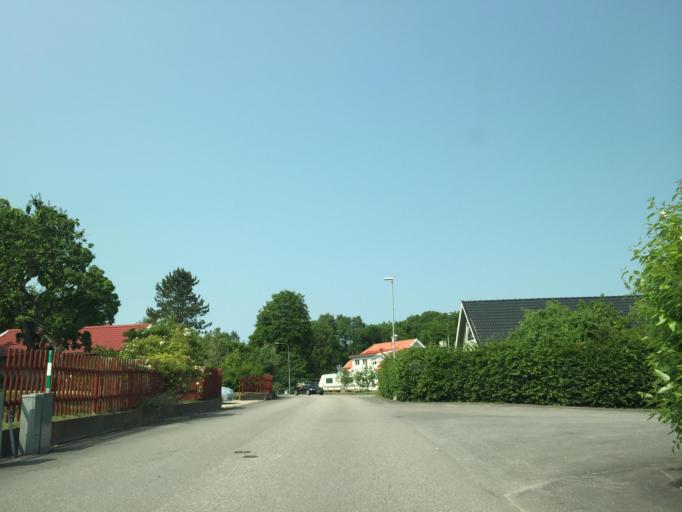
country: SE
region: Vaestra Goetaland
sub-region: Lilla Edets Kommun
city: Lilla Edet
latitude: 58.1800
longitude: 12.1081
